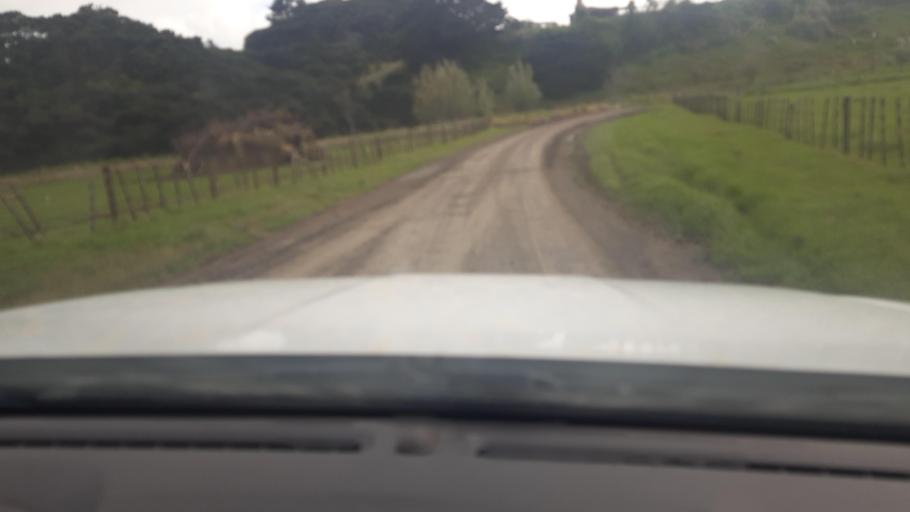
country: NZ
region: Northland
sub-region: Far North District
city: Ahipara
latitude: -35.2614
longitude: 173.1974
